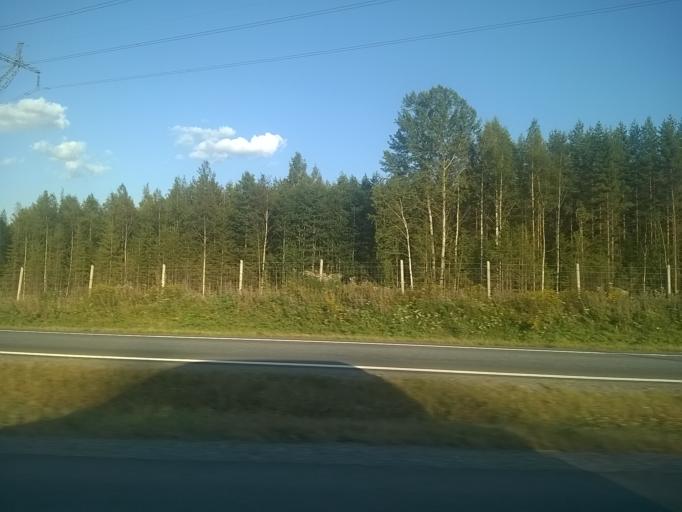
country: FI
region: Pirkanmaa
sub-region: Tampere
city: Tampere
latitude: 61.4482
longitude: 23.7657
